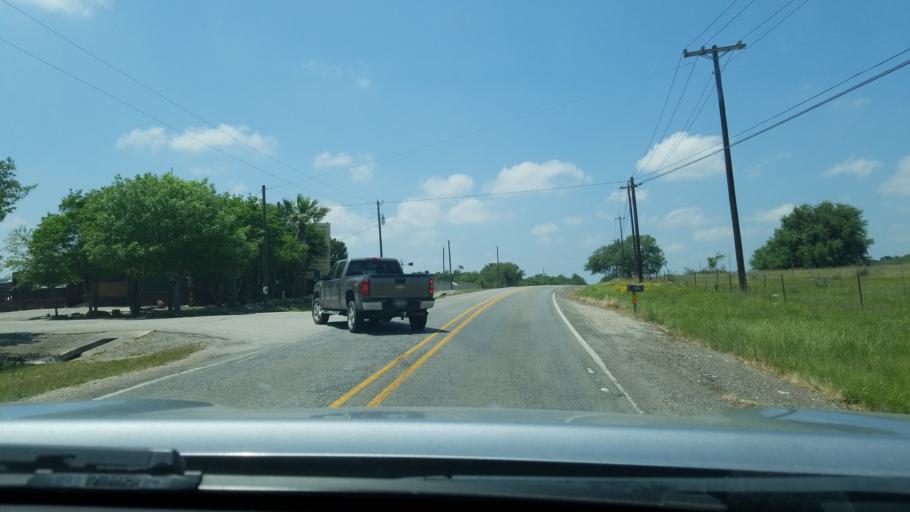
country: US
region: Texas
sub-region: Hays County
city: Woodcreek
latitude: 30.0365
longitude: -98.1827
